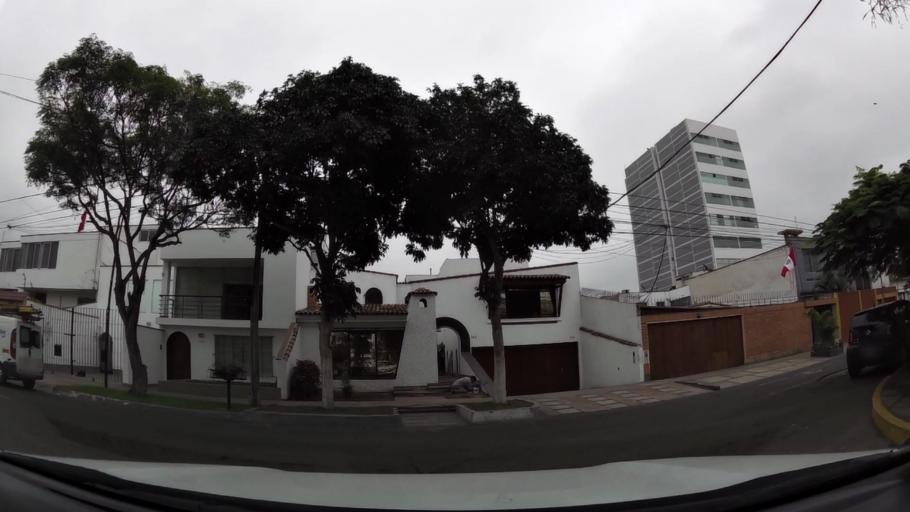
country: PE
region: Lima
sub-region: Lima
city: Surco
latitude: -12.1272
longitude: -77.0068
